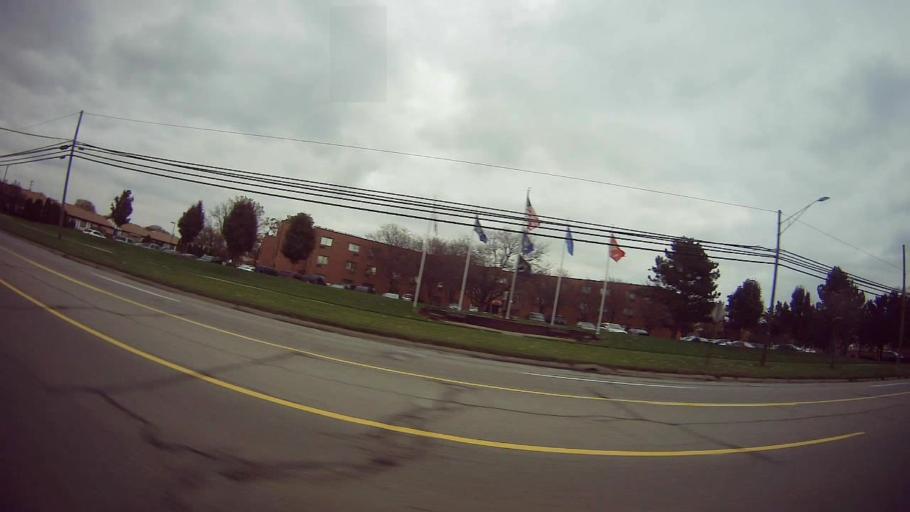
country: US
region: Michigan
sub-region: Macomb County
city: Center Line
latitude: 42.5125
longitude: -83.0072
